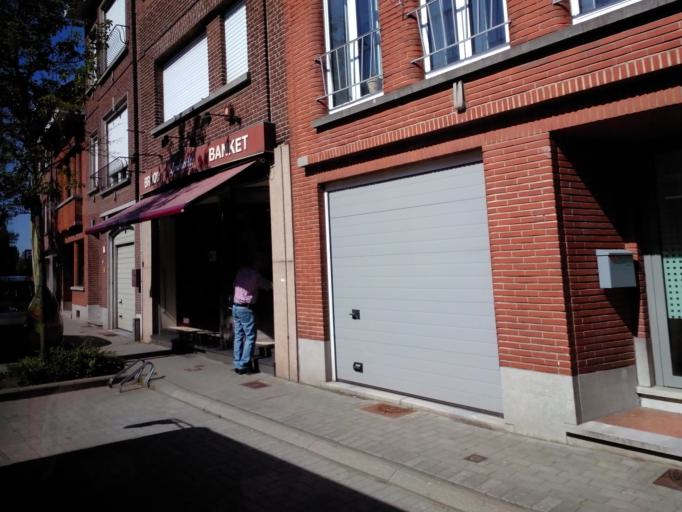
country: BE
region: Flanders
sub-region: Provincie Vlaams-Brabant
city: Leuven
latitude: 50.8864
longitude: 4.7191
